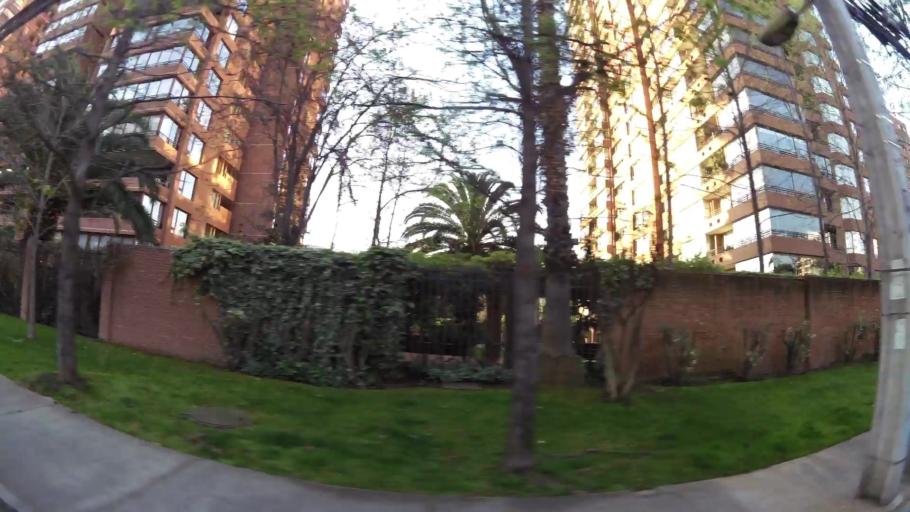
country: CL
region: Santiago Metropolitan
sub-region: Provincia de Santiago
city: Villa Presidente Frei, Nunoa, Santiago, Chile
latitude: -33.3959
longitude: -70.5625
